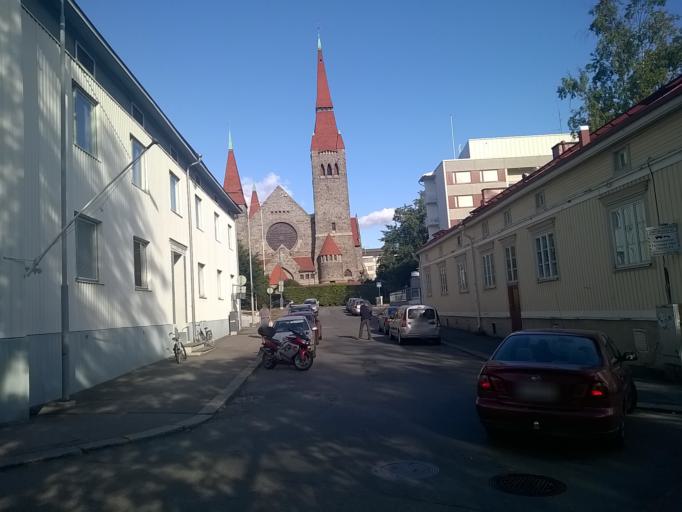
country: FI
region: Pirkanmaa
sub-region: Tampere
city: Tampere
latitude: 61.5025
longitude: 23.7672
